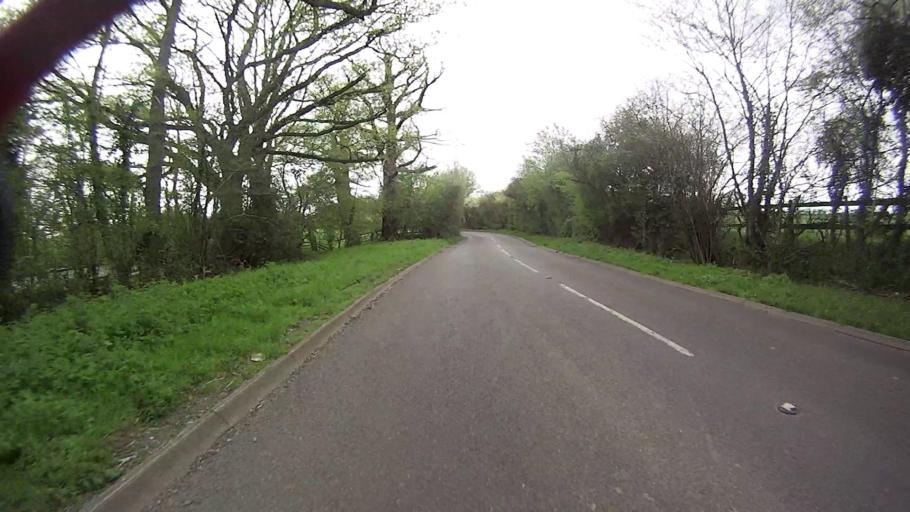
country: GB
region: England
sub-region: Surrey
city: Newdigate
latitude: 51.1273
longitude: -0.2789
